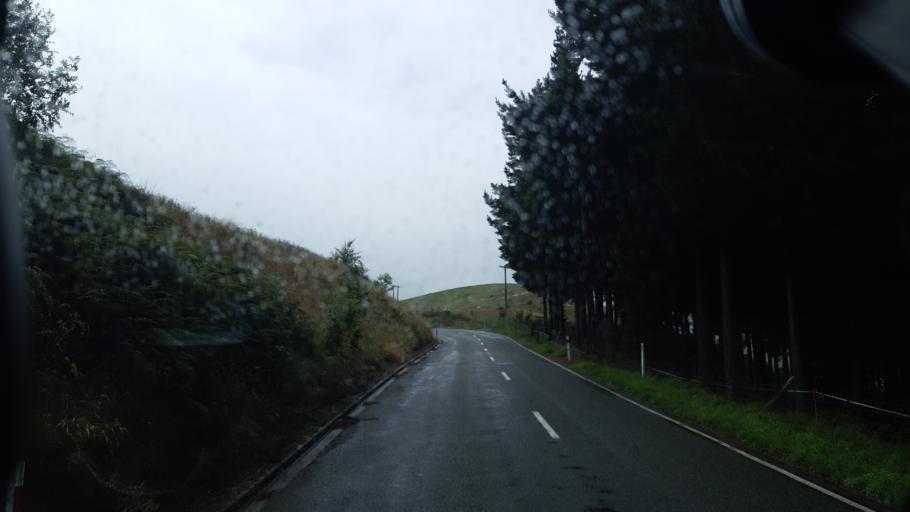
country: NZ
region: Canterbury
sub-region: Timaru District
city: Pleasant Point
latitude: -44.3165
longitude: 170.9456
